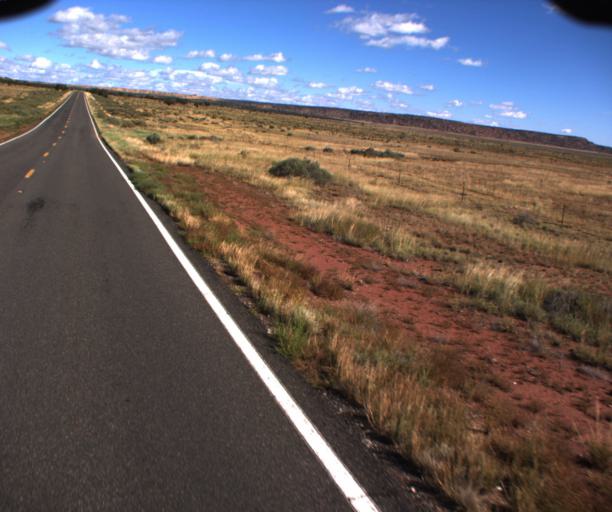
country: US
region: Arizona
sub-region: Apache County
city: Saint Johns
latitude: 34.7674
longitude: -109.2411
